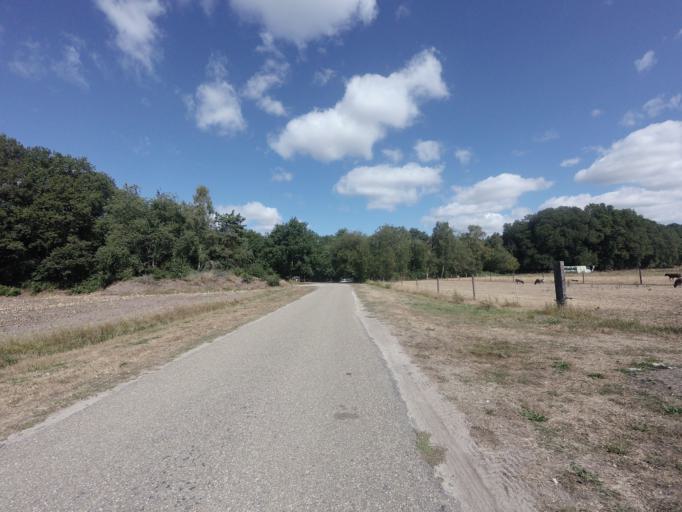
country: NL
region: North Brabant
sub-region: Gemeente Landerd
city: Schaijk
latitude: 51.7526
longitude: 5.6076
